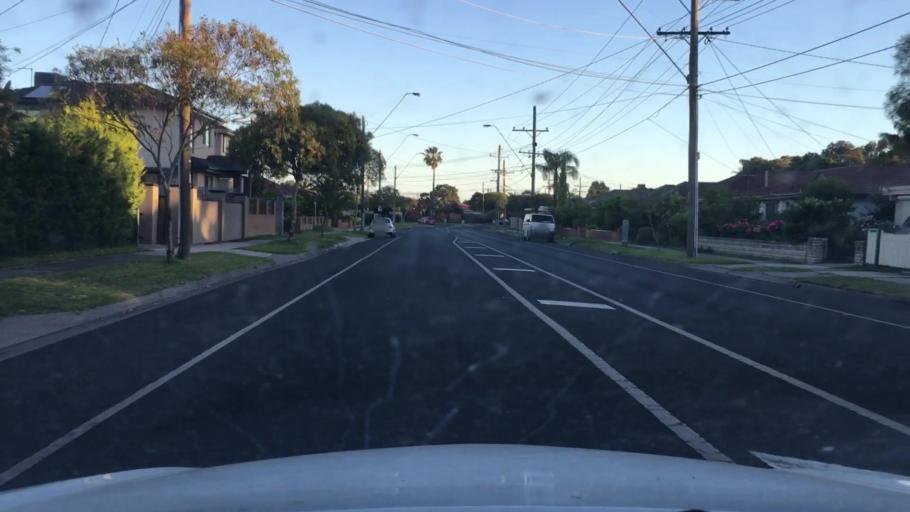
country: AU
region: Victoria
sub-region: Greater Dandenong
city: Keysborough
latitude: -37.9824
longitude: 145.1683
